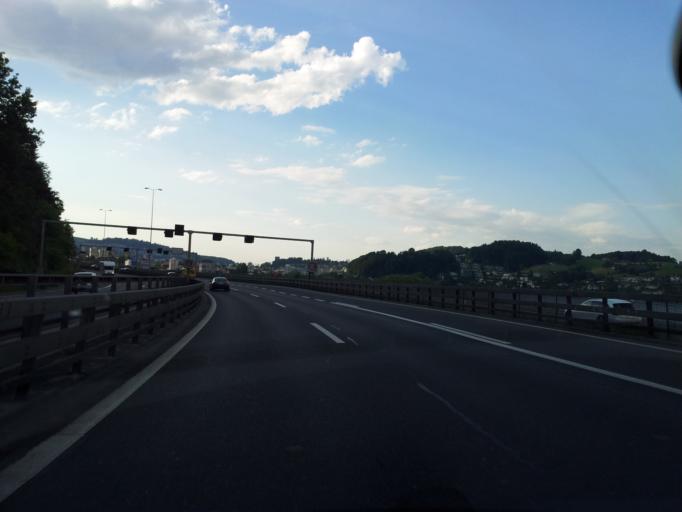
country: CH
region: Nidwalden
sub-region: Nidwalden
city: Hergiswil
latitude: 46.9999
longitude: 8.3114
